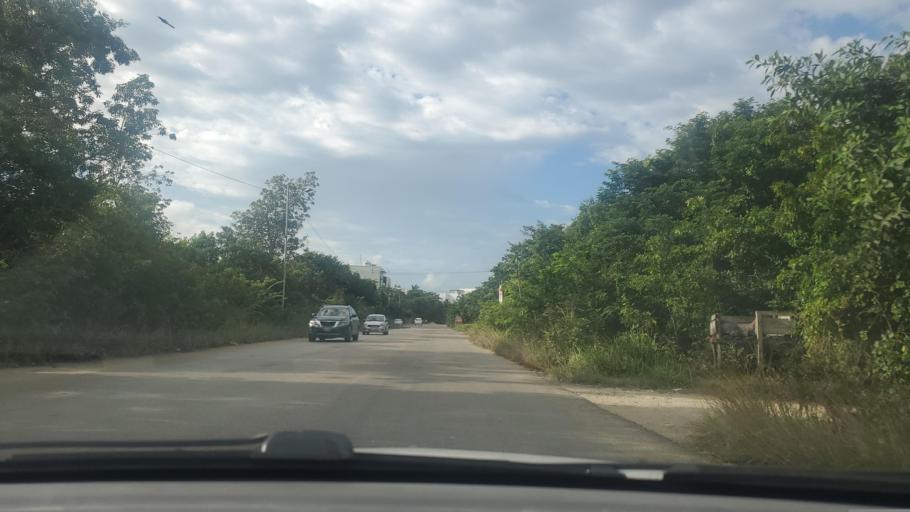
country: MX
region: Quintana Roo
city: Tulum
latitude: 20.2127
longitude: -87.4729
